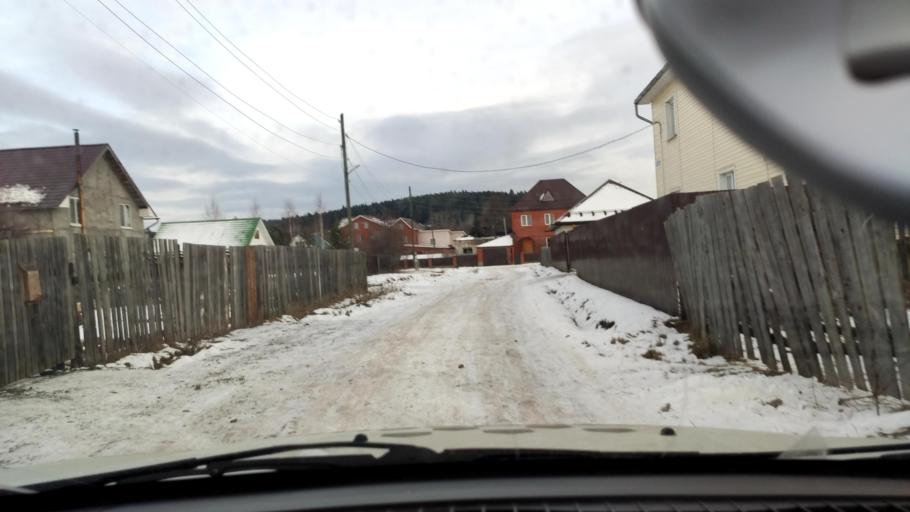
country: RU
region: Perm
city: Lobanovo
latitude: 57.8415
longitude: 56.3704
